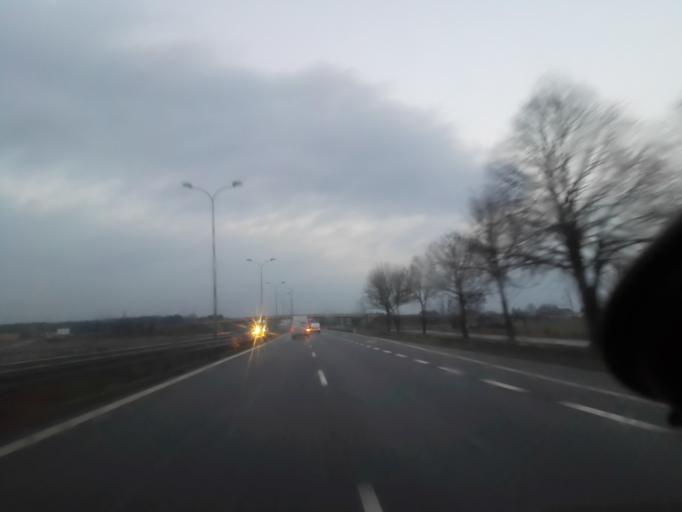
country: PL
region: Masovian Voivodeship
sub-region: Powiat wolominski
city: Dabrowka
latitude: 52.4908
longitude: 21.3620
